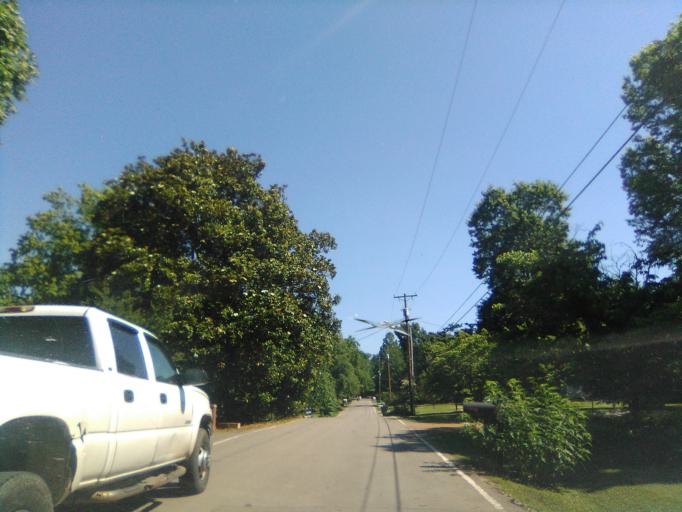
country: US
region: Tennessee
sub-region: Davidson County
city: Belle Meade
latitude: 36.1206
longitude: -86.8321
